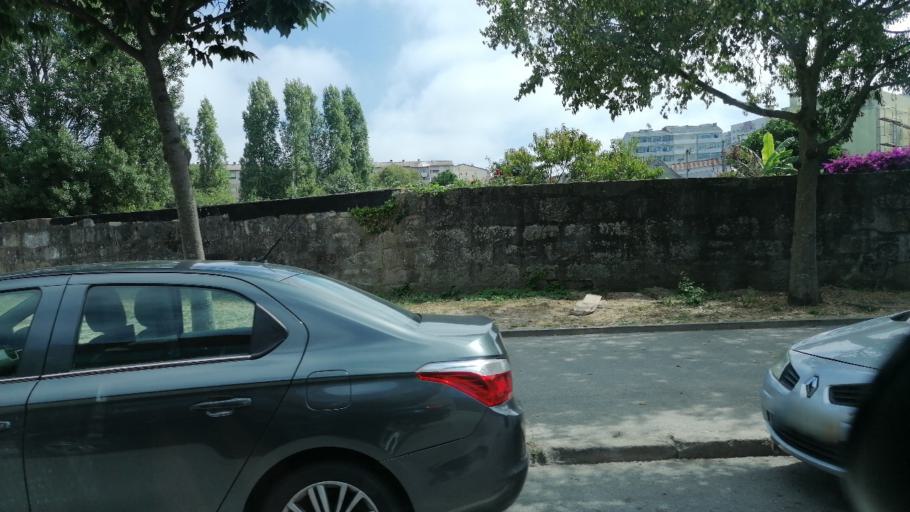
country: PT
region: Porto
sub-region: Matosinhos
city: Senhora da Hora
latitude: 41.1722
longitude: -8.6426
